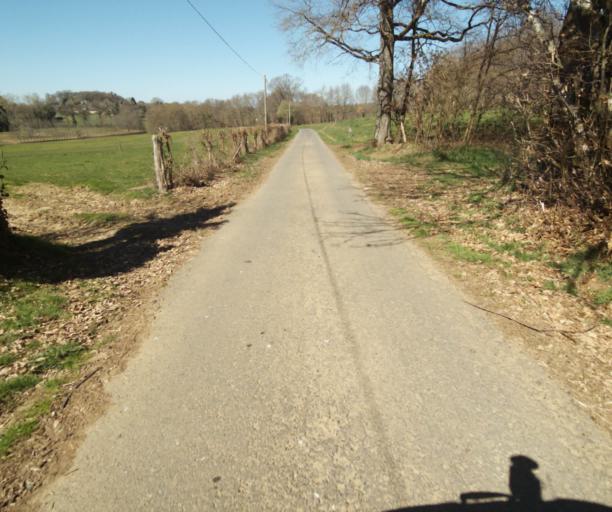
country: FR
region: Limousin
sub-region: Departement de la Correze
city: Saint-Clement
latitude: 45.3903
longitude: 1.6505
